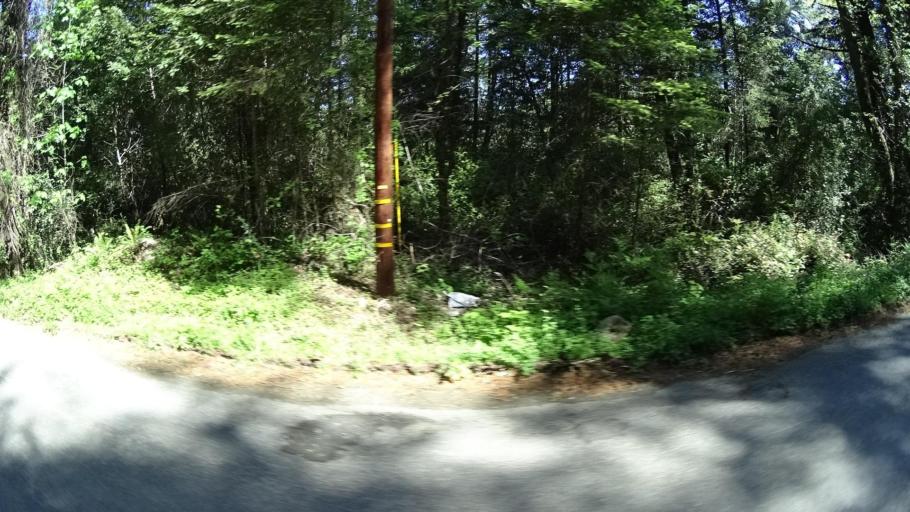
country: US
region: California
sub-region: Humboldt County
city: Rio Dell
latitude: 40.2296
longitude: -124.1493
